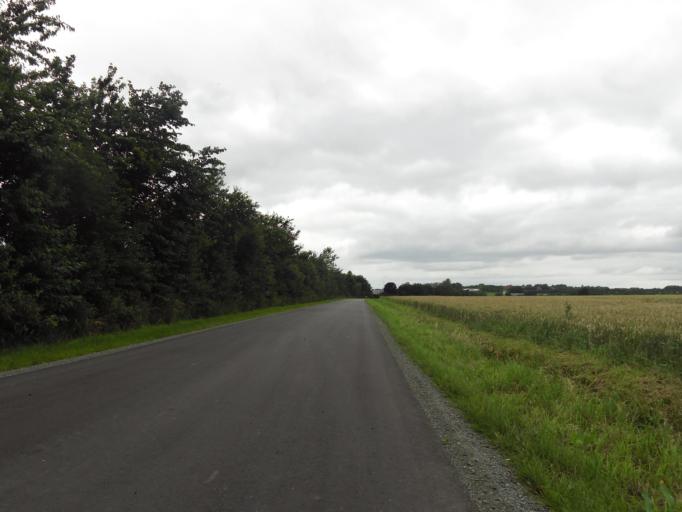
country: DK
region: South Denmark
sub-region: Haderslev Kommune
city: Gram
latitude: 55.2594
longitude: 9.1606
